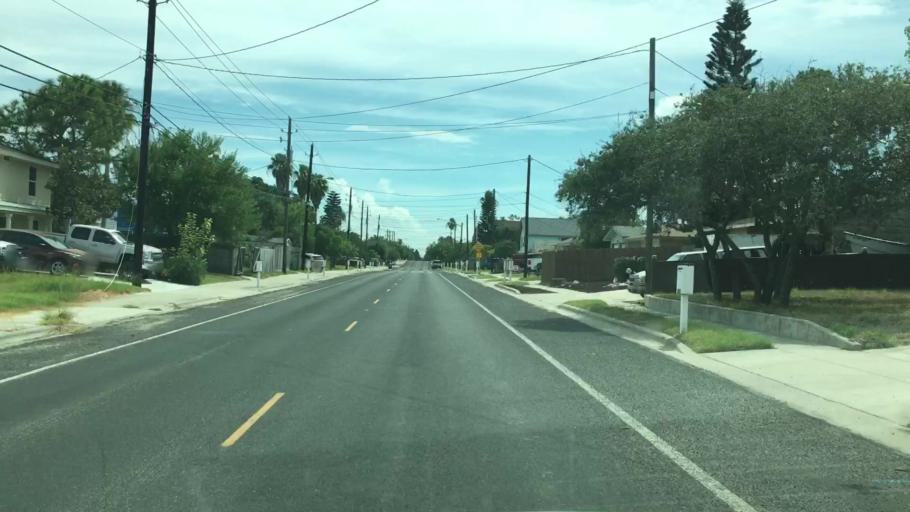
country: US
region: Texas
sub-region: Nueces County
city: Corpus Christi
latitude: 27.6308
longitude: -97.2908
